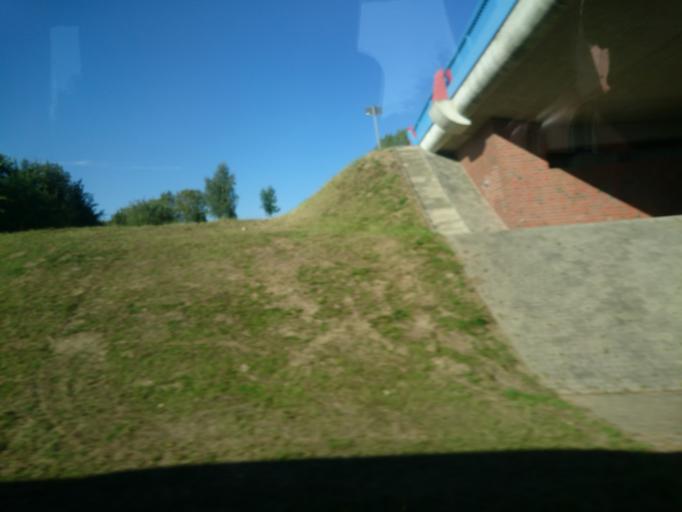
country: DE
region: Mecklenburg-Vorpommern
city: Anklam
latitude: 53.8347
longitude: 13.7171
